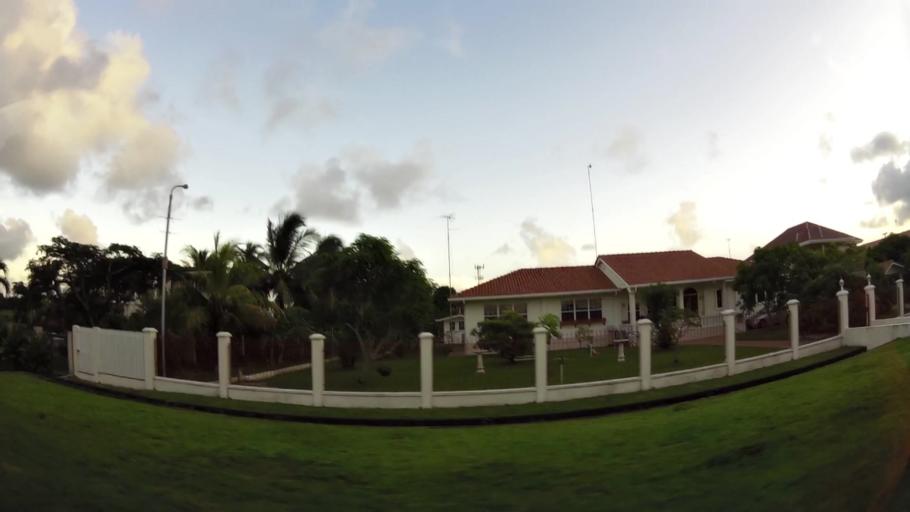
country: GY
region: Demerara-Mahaica
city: Georgetown
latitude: 6.8067
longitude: -58.1018
